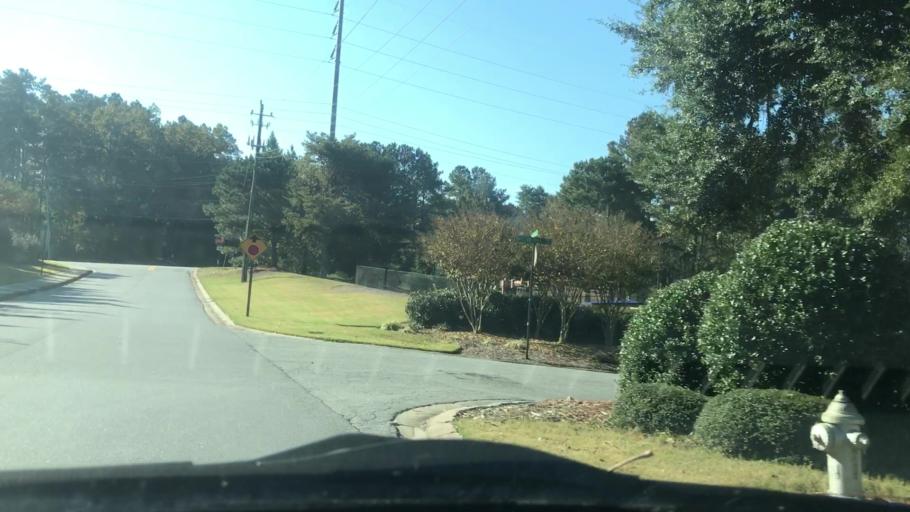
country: US
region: Georgia
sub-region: Fulton County
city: Roswell
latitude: 34.0021
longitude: -84.4032
